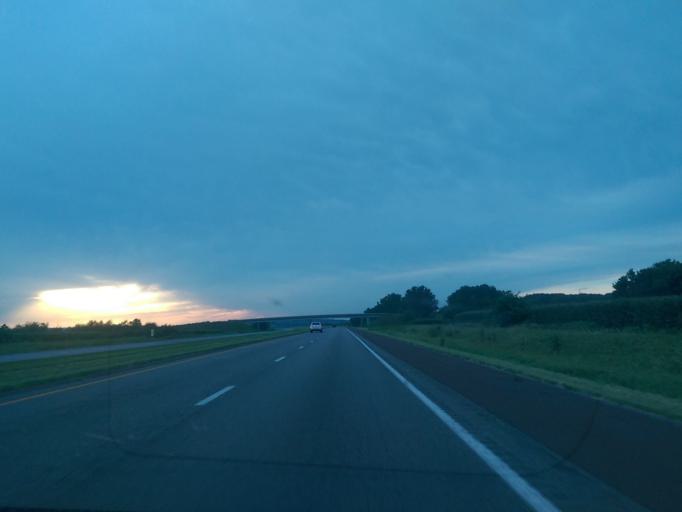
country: US
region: Missouri
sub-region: Holt County
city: Mound City
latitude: 40.1776
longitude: -95.3096
